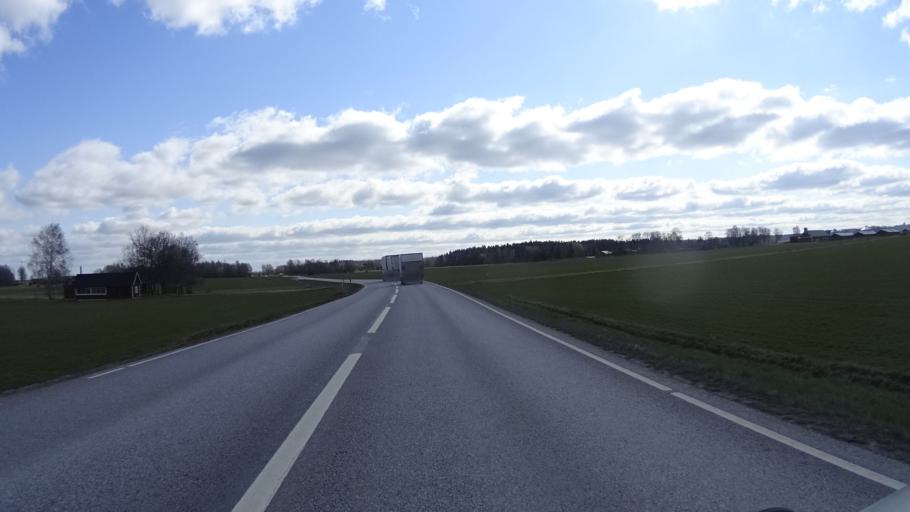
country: SE
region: OEstergoetland
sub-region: Mjolby Kommun
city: Mantorp
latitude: 58.3777
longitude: 15.2599
